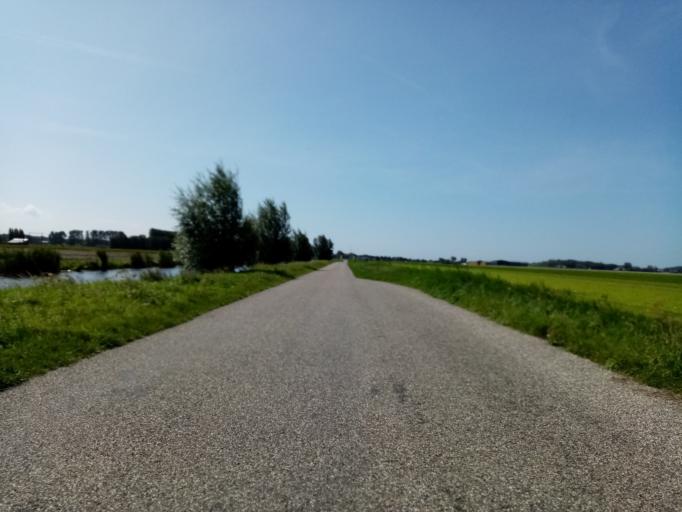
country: NL
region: South Holland
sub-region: Gemeente Lisse
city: Lisse
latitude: 52.2886
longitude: 4.5460
